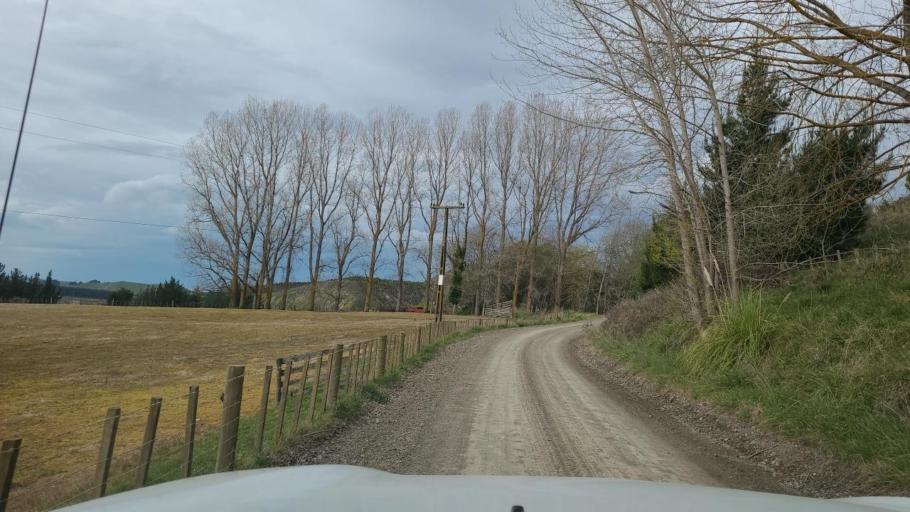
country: NZ
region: Hawke's Bay
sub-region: Napier City
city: Napier
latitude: -39.1804
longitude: 176.9737
